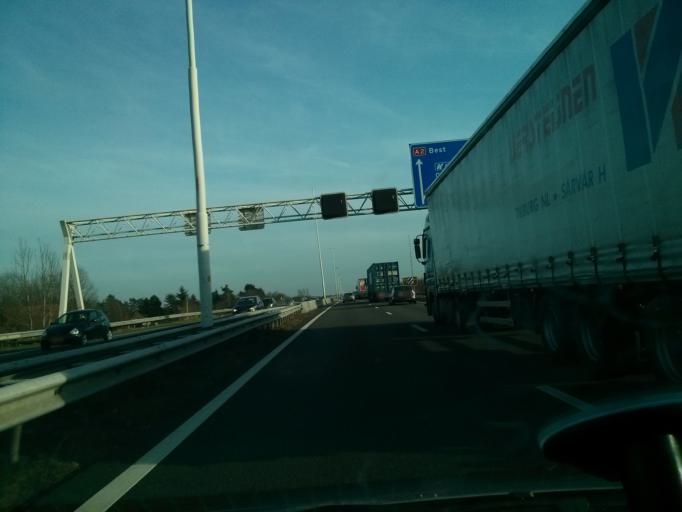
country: NL
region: North Brabant
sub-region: Gemeente Oirschot
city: Oirschot
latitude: 51.5010
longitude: 5.2956
